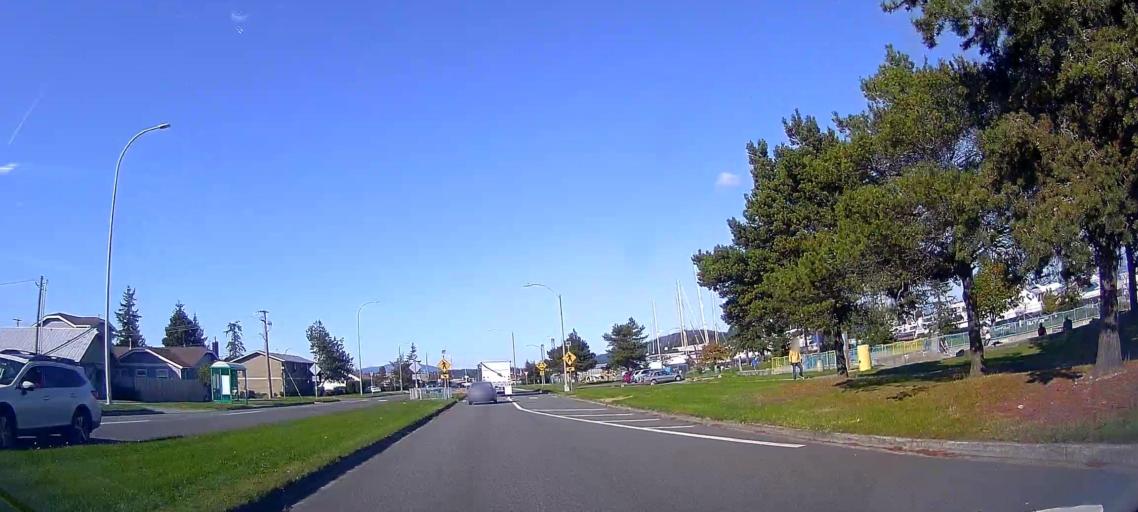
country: US
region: Washington
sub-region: Skagit County
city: Anacortes
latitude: 48.5031
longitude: -122.6095
